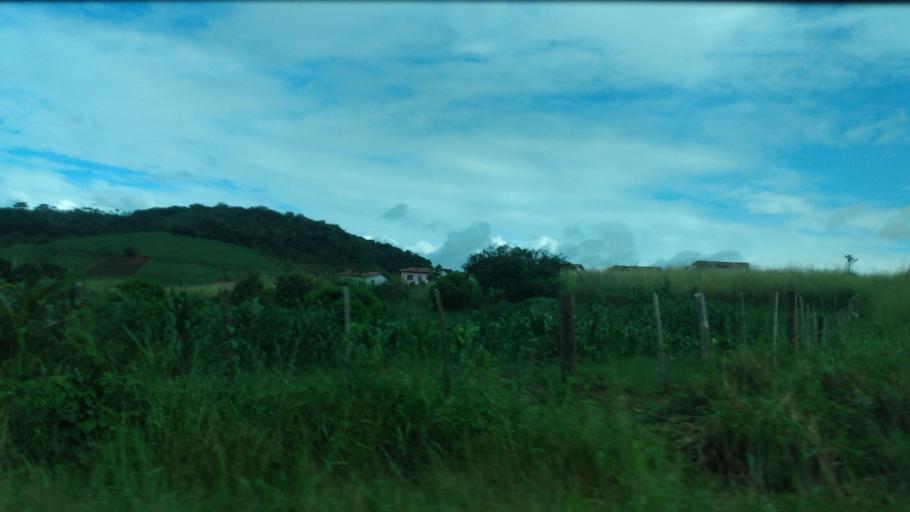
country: BR
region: Pernambuco
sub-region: Catende
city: Catende
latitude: -8.7035
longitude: -35.7563
